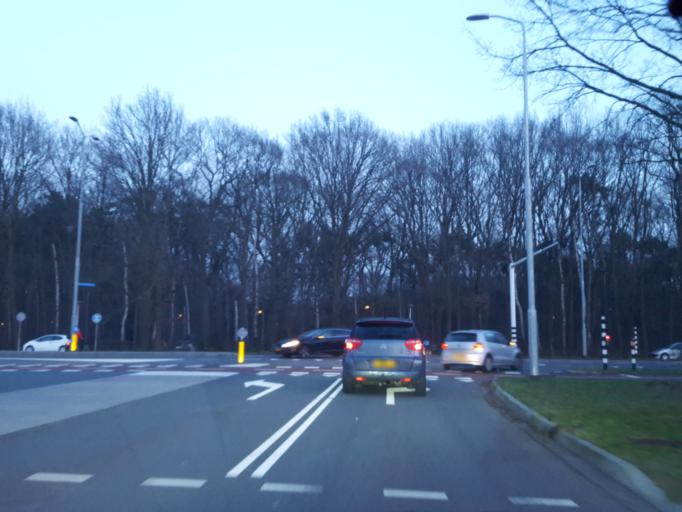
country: NL
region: North Brabant
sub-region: Gemeente Eindhoven
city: Eindhoven
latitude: 51.4074
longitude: 5.4806
